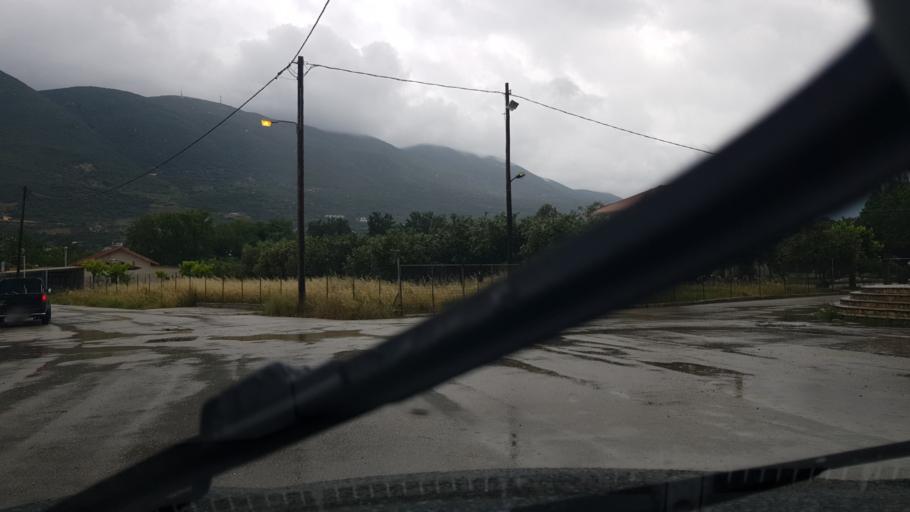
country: GR
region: Ionian Islands
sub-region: Lefkada
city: Nidri
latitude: 38.6291
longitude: 20.6063
